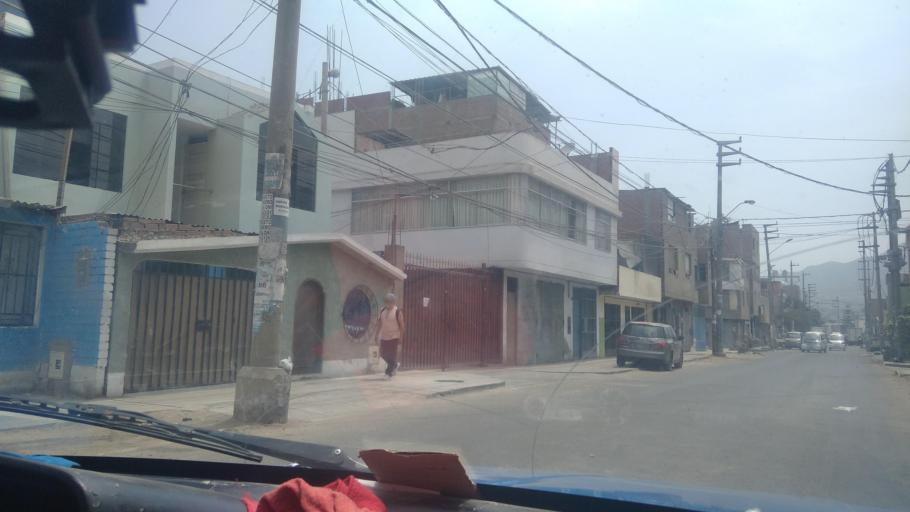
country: PE
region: Lima
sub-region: Lima
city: Independencia
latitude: -11.9793
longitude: -77.0089
